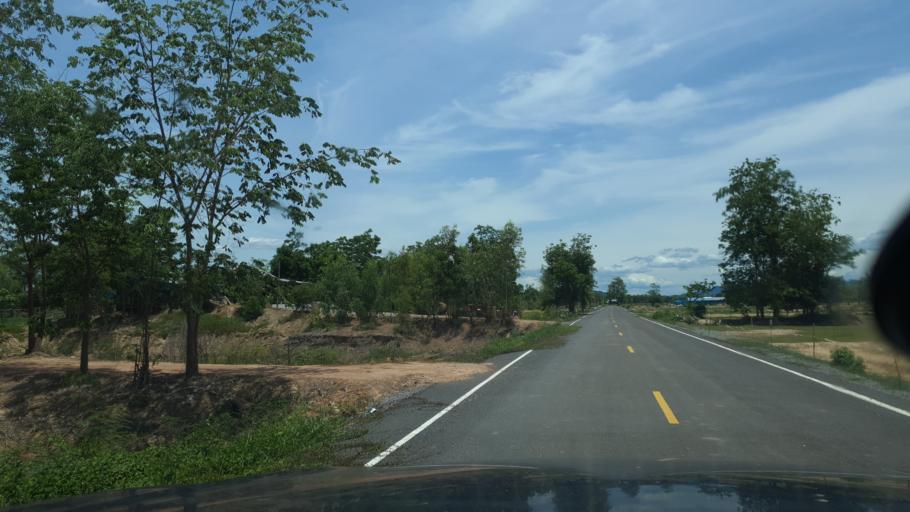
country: TH
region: Sukhothai
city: Ban Dan Lan Hoi
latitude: 17.1507
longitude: 99.6437
